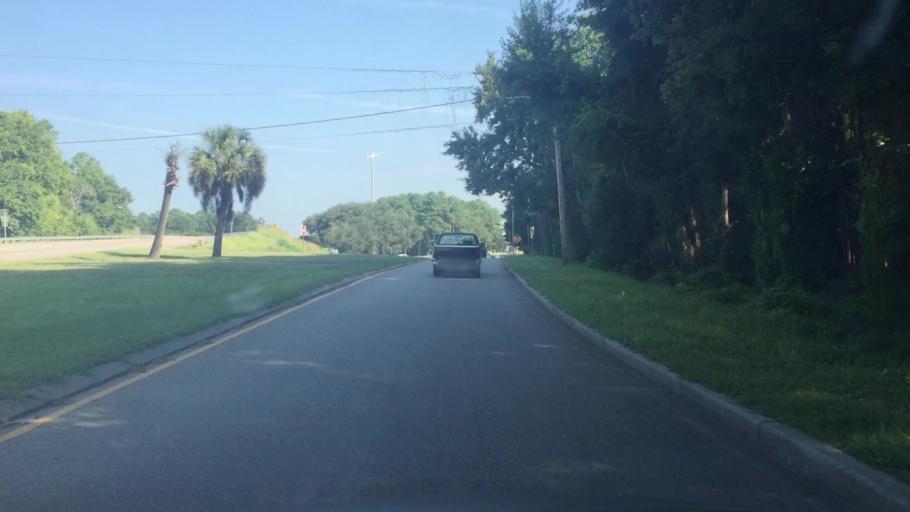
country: US
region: South Carolina
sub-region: Horry County
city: North Myrtle Beach
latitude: 33.8454
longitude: -78.6512
